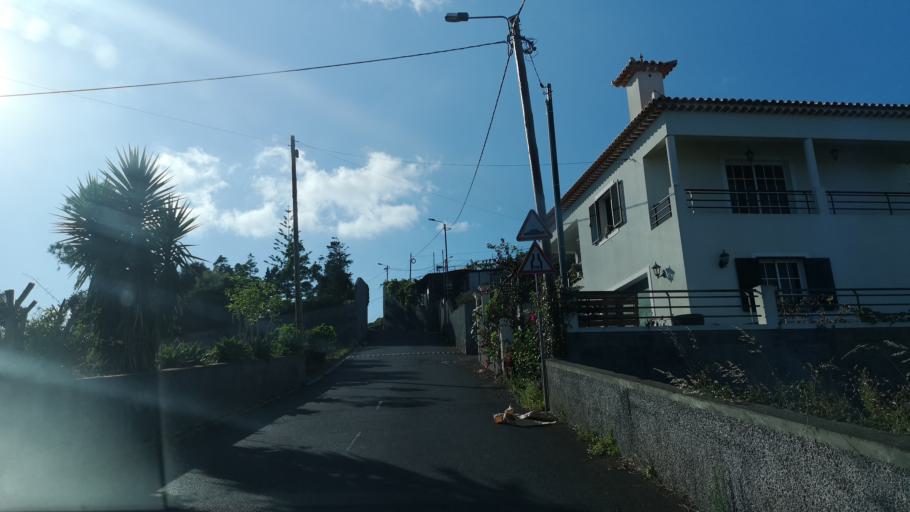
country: PT
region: Madeira
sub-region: Santa Cruz
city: Camacha
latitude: 32.6563
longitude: -16.8346
